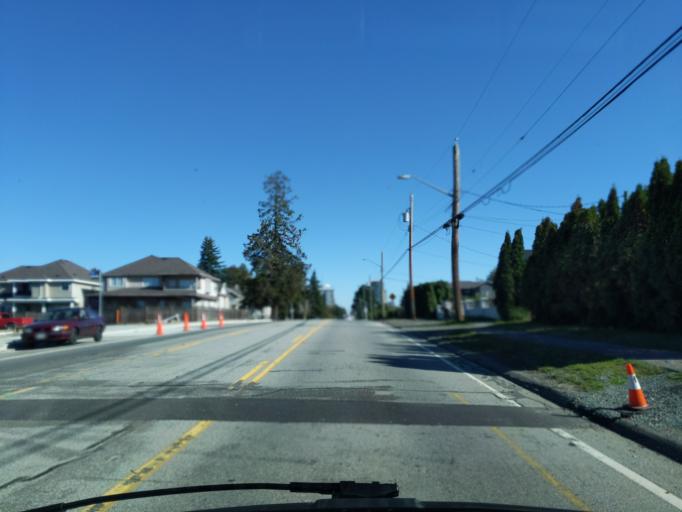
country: CA
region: British Columbia
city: New Westminster
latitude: 49.1990
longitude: -122.8636
